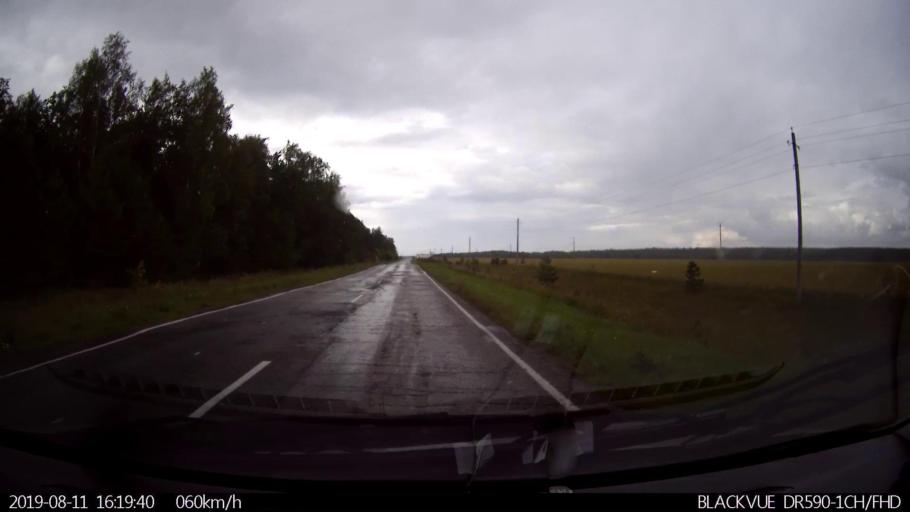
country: RU
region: Ulyanovsk
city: Mayna
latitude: 54.0657
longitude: 47.6063
